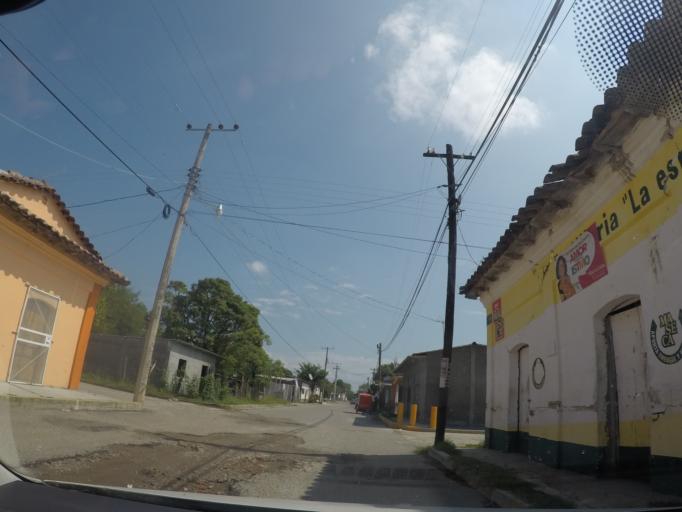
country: MX
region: Oaxaca
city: San Francisco Ixhuatan
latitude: 16.3976
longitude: -94.4585
